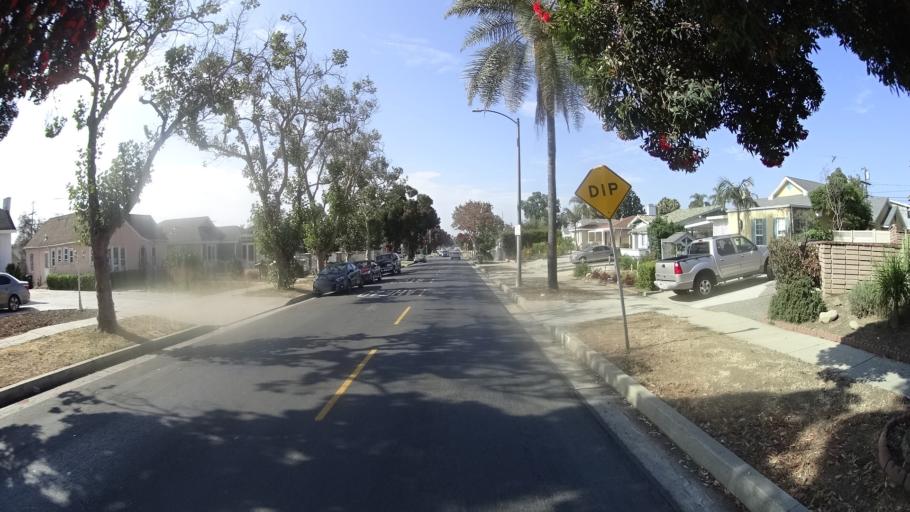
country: US
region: California
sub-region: Los Angeles County
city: View Park-Windsor Hills
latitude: 33.9940
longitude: -118.3355
